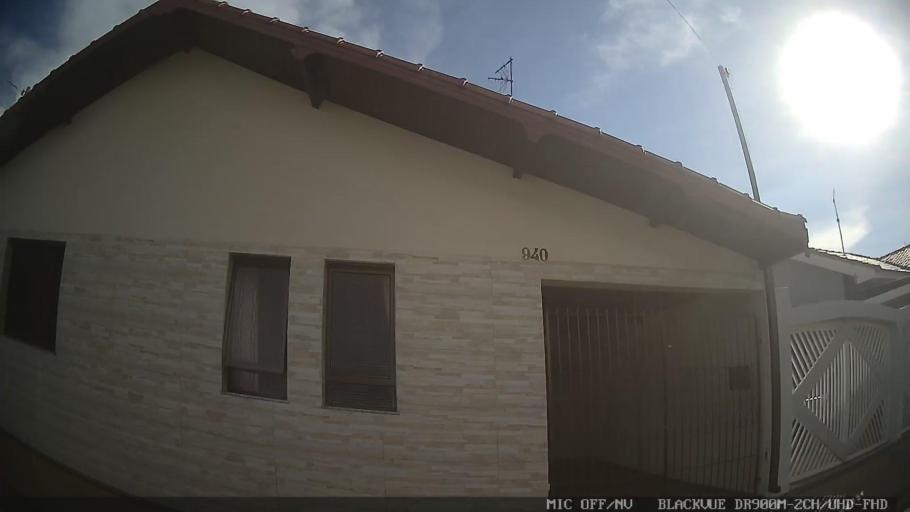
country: BR
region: Sao Paulo
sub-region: Laranjal Paulista
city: Laranjal Paulista
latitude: -23.0870
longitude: -47.7834
